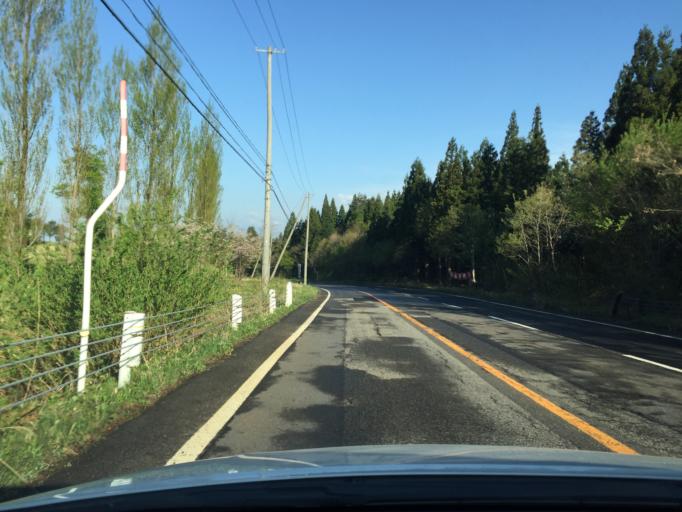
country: JP
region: Fukushima
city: Inawashiro
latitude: 37.6609
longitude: 140.0208
